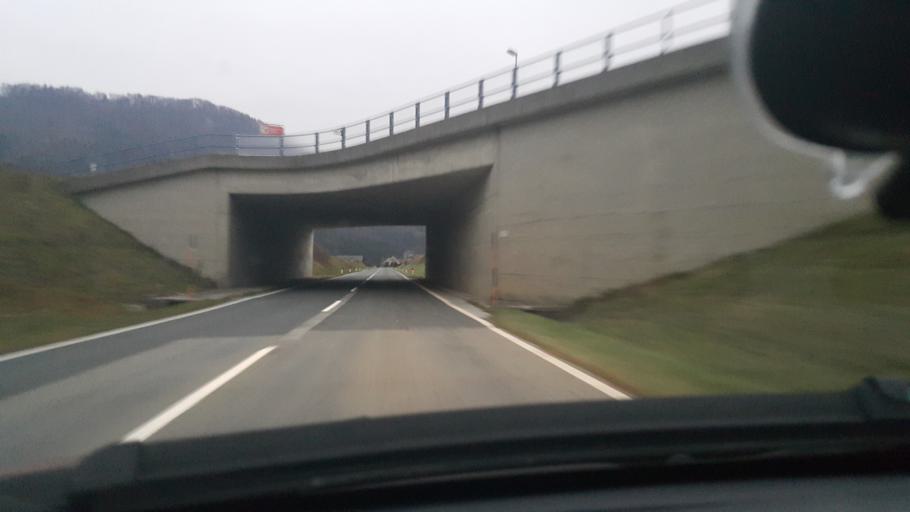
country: AT
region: Carinthia
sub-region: Politischer Bezirk Volkermarkt
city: Ruden
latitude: 46.6598
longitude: 14.8236
